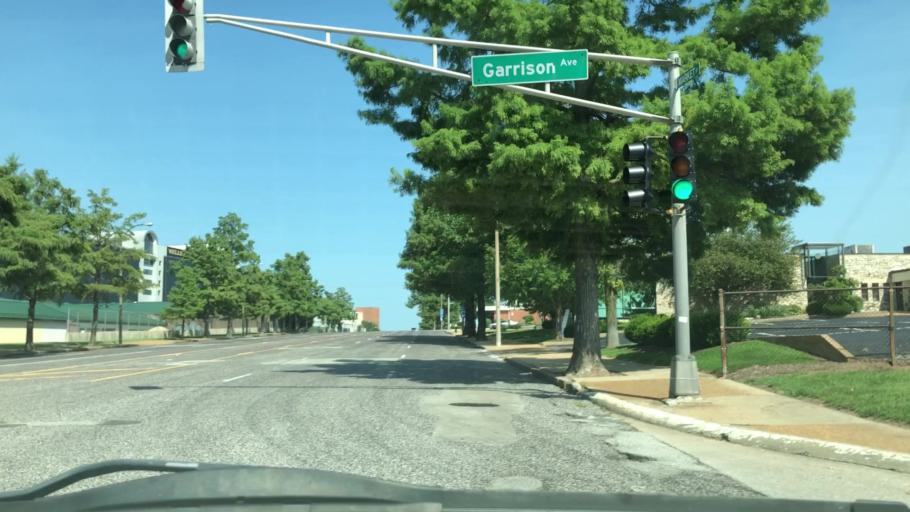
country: US
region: Missouri
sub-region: City of Saint Louis
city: St. Louis
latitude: 38.6309
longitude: -90.2233
